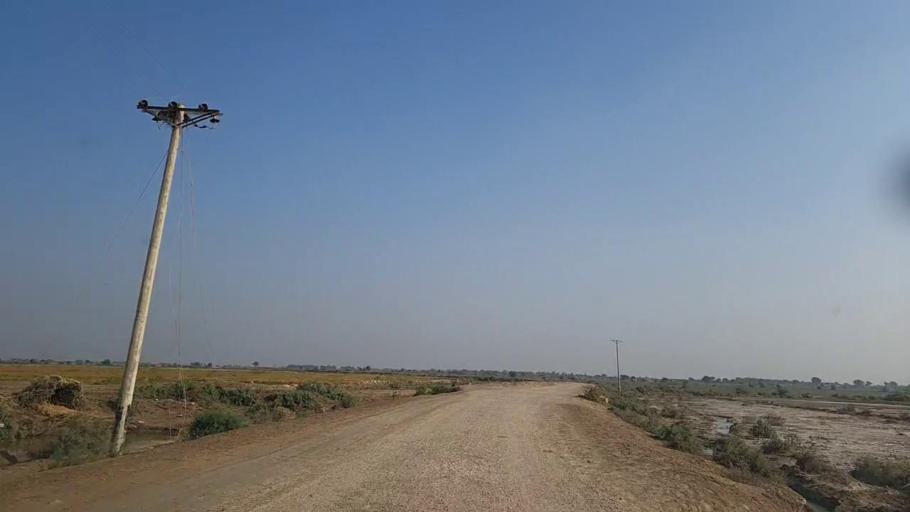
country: PK
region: Sindh
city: Jati
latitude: 24.4613
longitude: 68.2843
